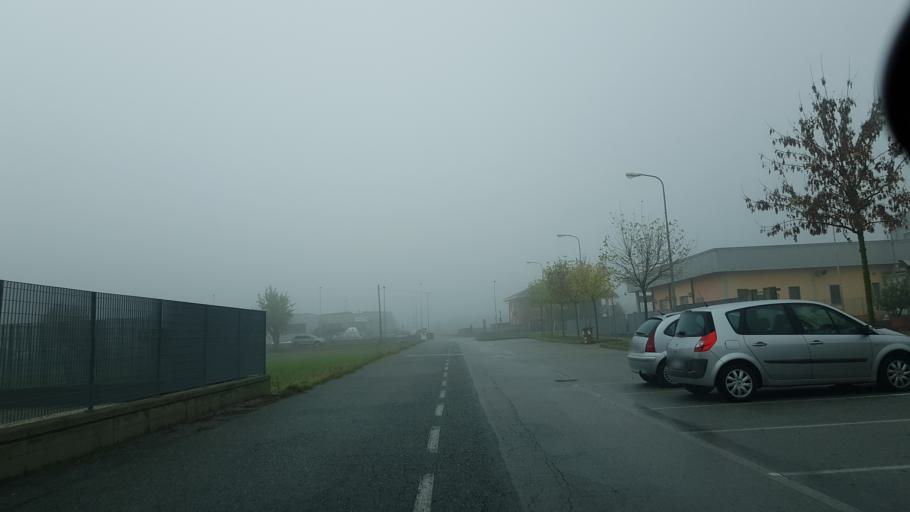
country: IT
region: Piedmont
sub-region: Provincia di Cuneo
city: Villafalletto
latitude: 44.5442
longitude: 7.5458
